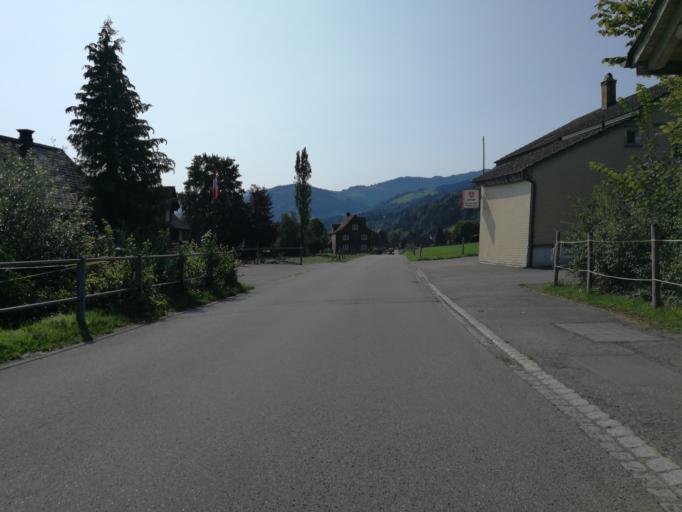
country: CH
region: Saint Gallen
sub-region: Wahlkreis Toggenburg
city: Ebnat-Kappel
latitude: 47.2763
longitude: 9.0999
